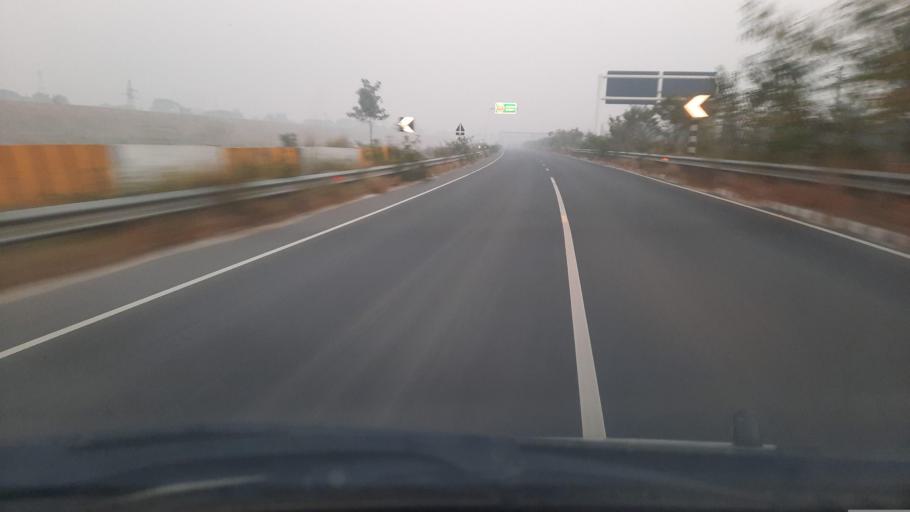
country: BD
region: Dhaka
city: Dohar
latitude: 23.5302
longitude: 90.2901
